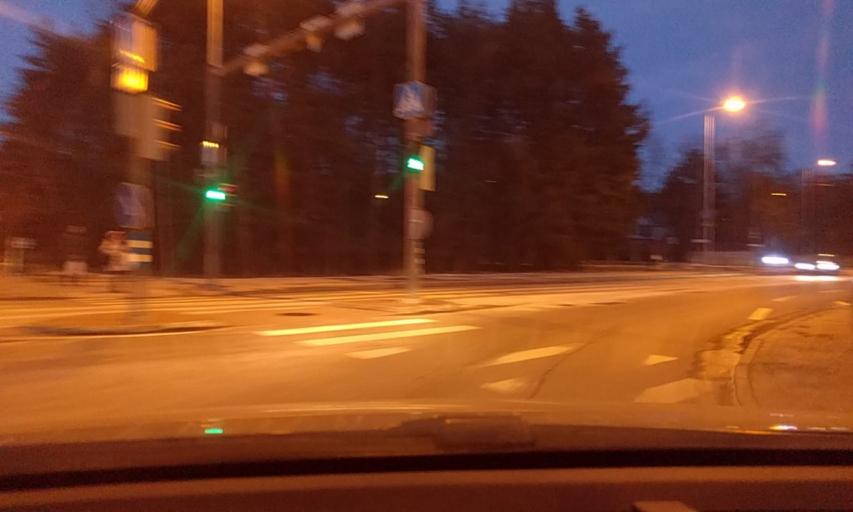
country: EE
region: Harju
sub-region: Viimsi vald
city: Viimsi
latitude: 59.4742
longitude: 24.8378
